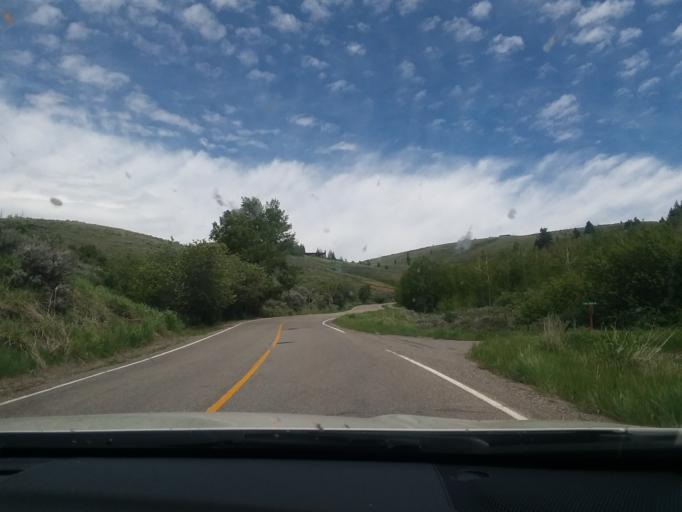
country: US
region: Wyoming
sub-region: Teton County
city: Jackson
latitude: 43.4950
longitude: -110.7812
